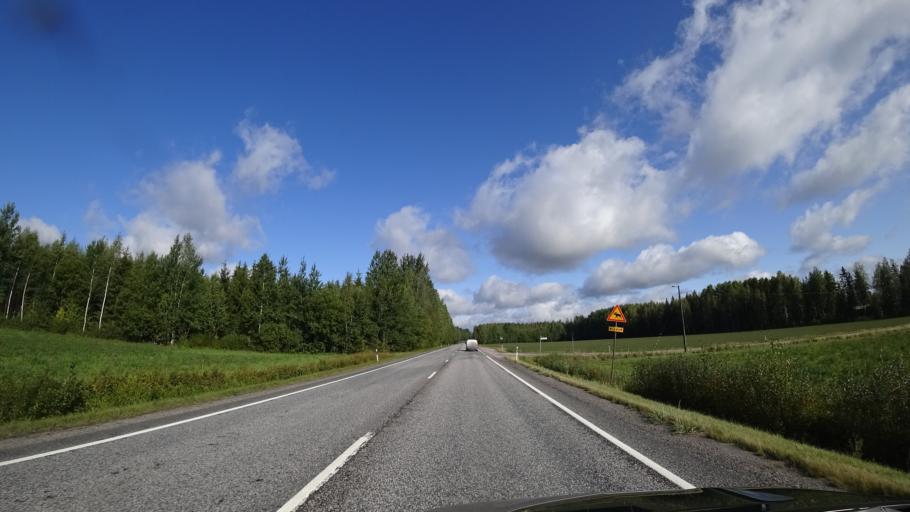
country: FI
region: Uusimaa
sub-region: Helsinki
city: Tuusula
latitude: 60.4712
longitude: 24.9431
